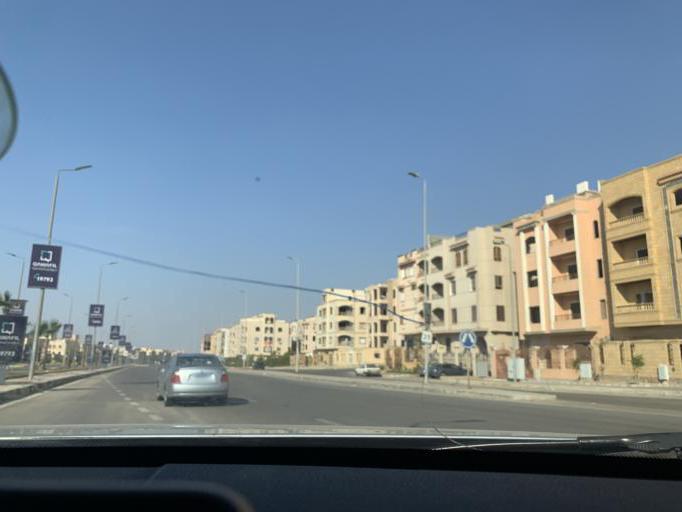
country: EG
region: Muhafazat al Qahirah
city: Cairo
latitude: 30.0004
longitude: 31.4689
